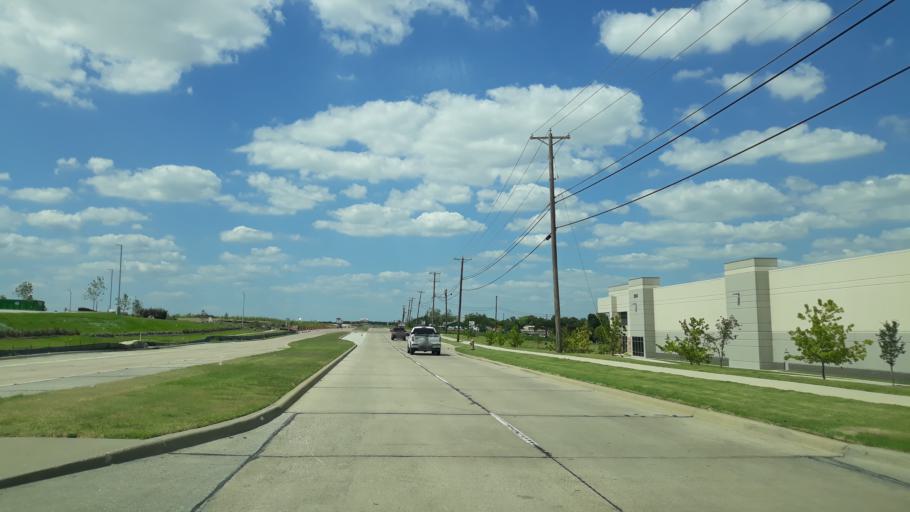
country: US
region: Texas
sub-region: Tarrant County
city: Euless
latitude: 32.8436
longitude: -97.0217
